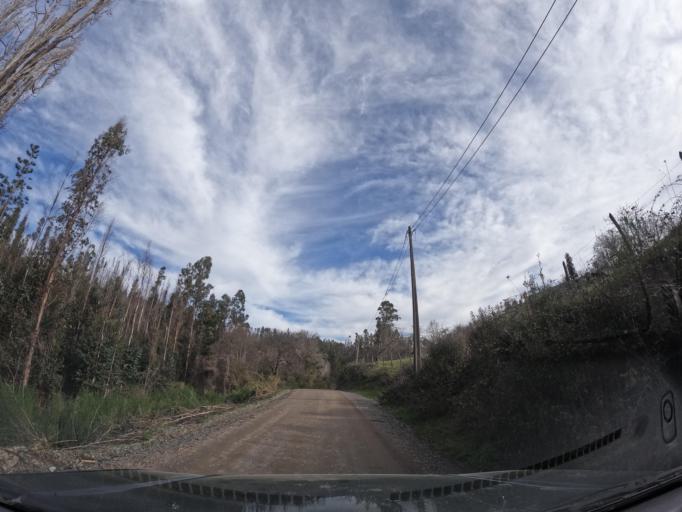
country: CL
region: Biobio
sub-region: Provincia de Concepcion
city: Chiguayante
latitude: -37.0141
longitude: -72.9092
